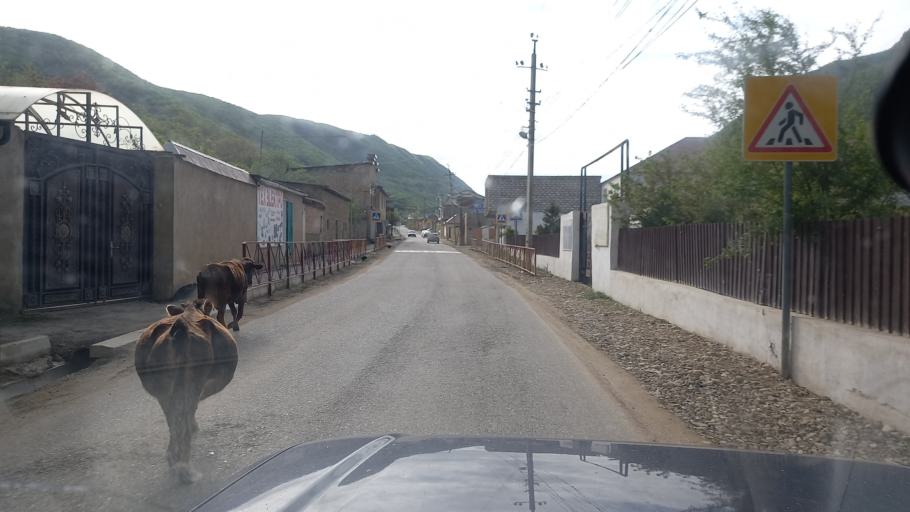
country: RU
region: Dagestan
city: Khuchni
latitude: 41.9620
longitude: 47.9567
